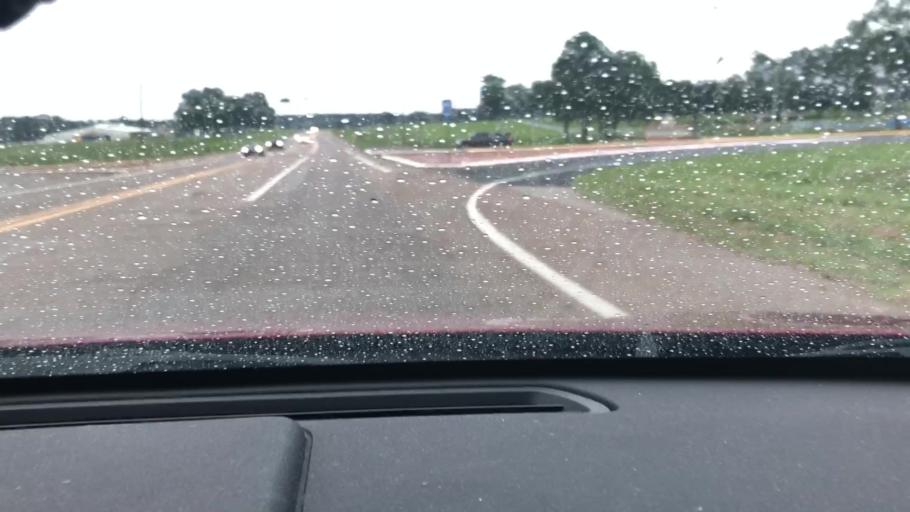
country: US
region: Arkansas
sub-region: Columbia County
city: Magnolia
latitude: 33.2973
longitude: -93.2375
